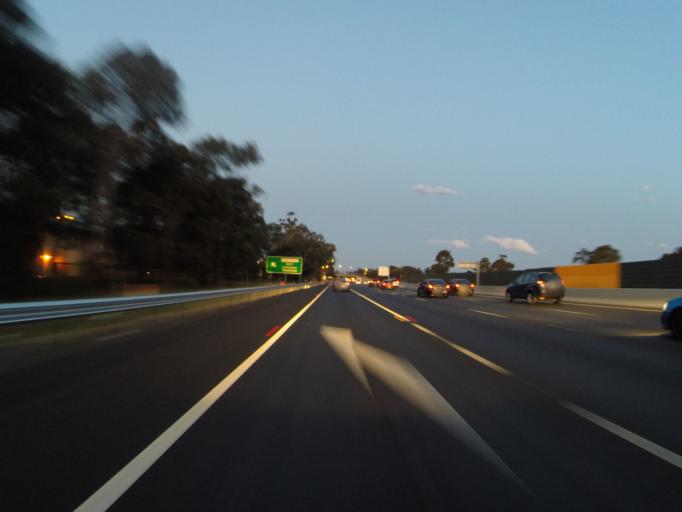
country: AU
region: New South Wales
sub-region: Fairfield
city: Liverpool
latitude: -33.9411
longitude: 150.9365
